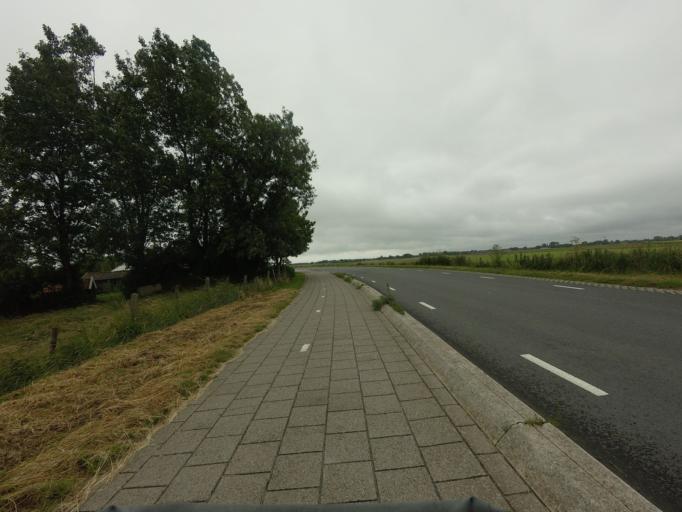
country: NL
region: North Holland
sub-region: Gemeente Schagen
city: Schagen
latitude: 52.8079
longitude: 4.8022
